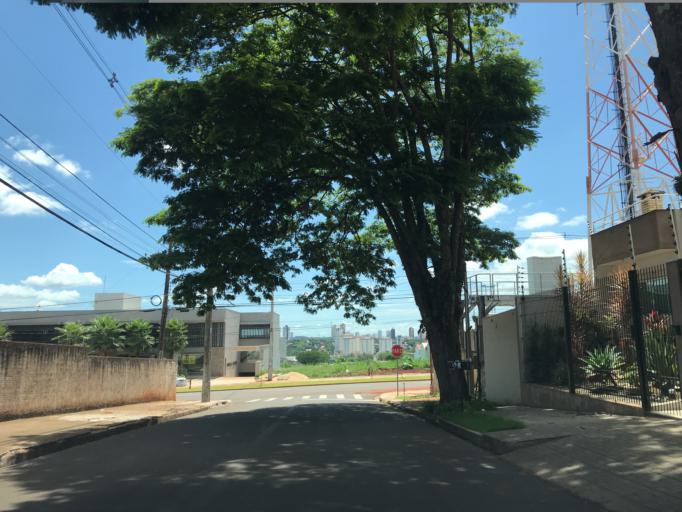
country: BR
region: Parana
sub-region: Maringa
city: Maringa
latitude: -23.4413
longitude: -51.9564
